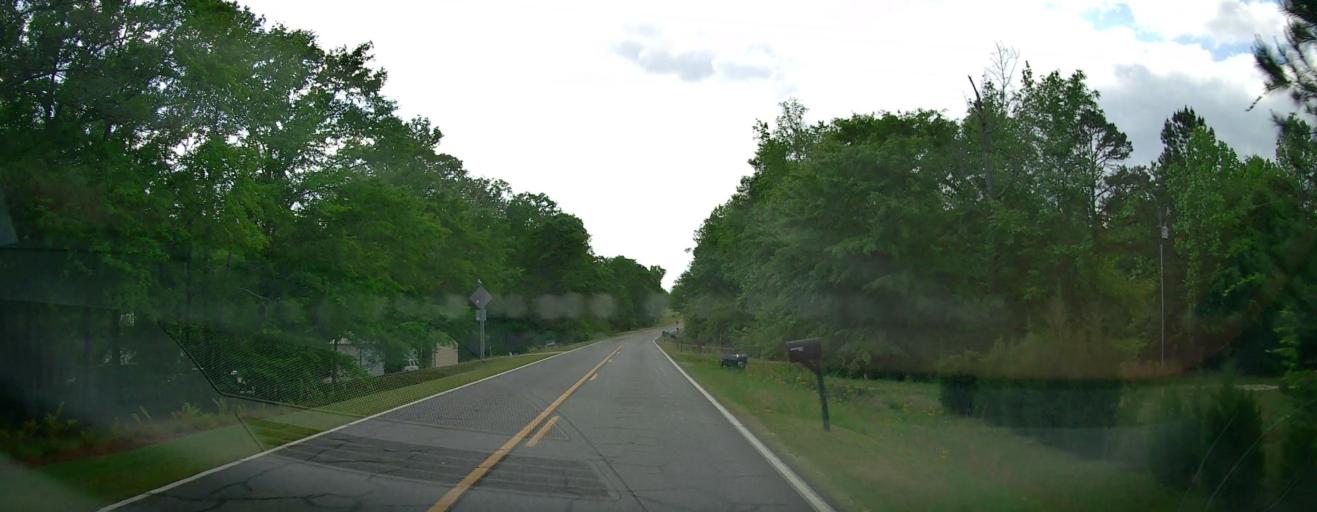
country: US
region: Georgia
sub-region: Baldwin County
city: Hardwick
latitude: 33.0609
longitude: -83.1336
